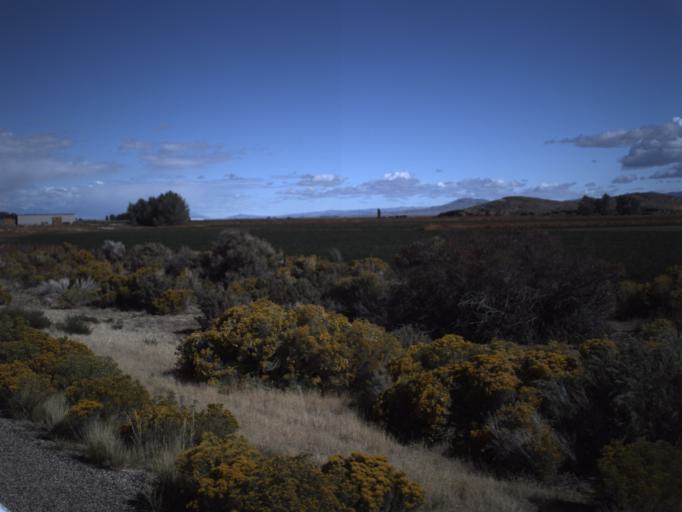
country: US
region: Nevada
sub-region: White Pine County
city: McGill
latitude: 38.9161
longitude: -114.0279
